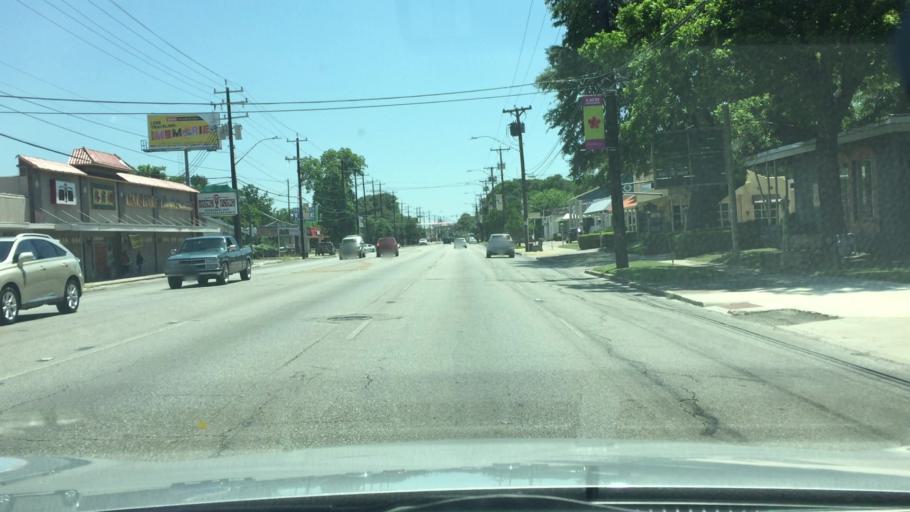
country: US
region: Texas
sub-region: Bexar County
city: Terrell Hills
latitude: 29.4606
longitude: -98.4672
